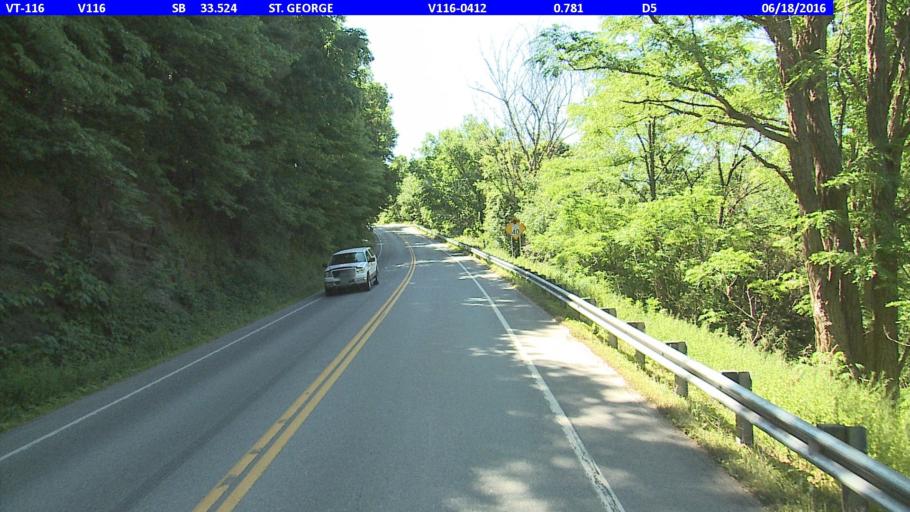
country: US
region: Vermont
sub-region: Chittenden County
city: Hinesburg
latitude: 44.3746
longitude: -73.1343
